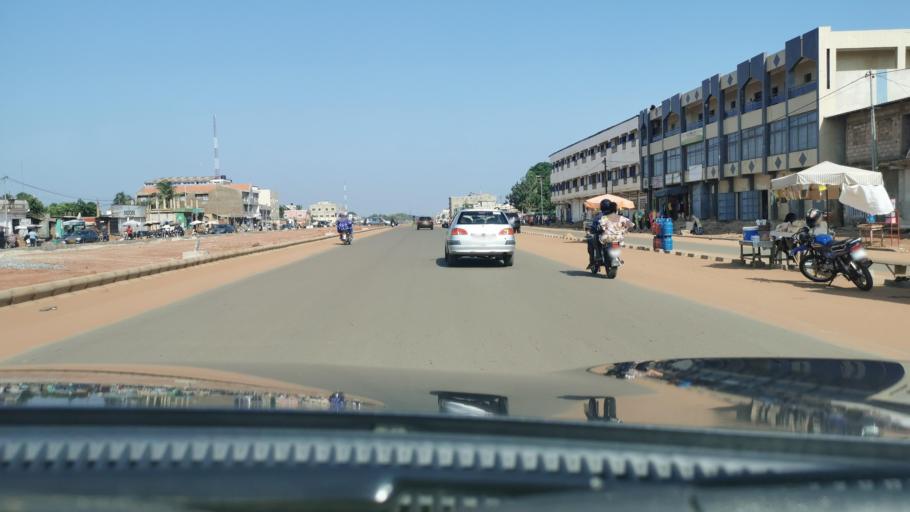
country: TG
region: Maritime
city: Lome
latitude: 6.2036
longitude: 1.1451
